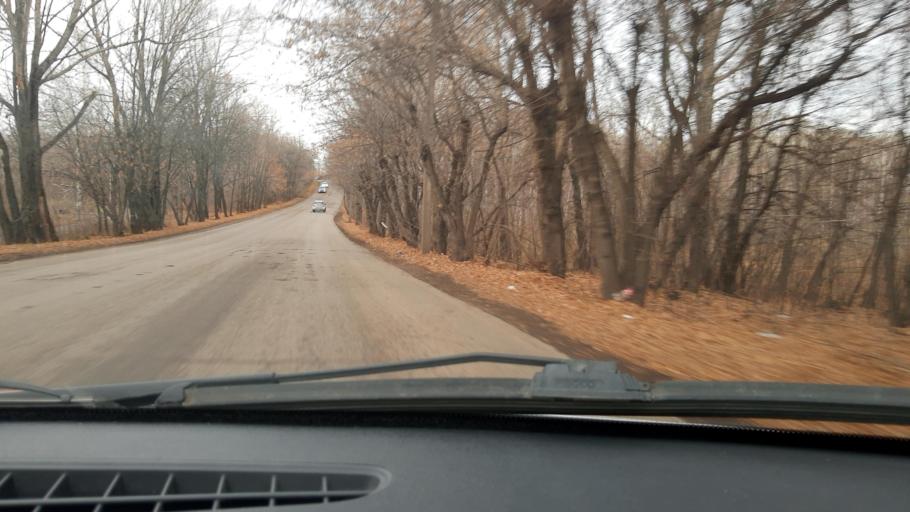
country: RU
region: Bashkortostan
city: Avdon
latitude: 54.7019
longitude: 55.8159
